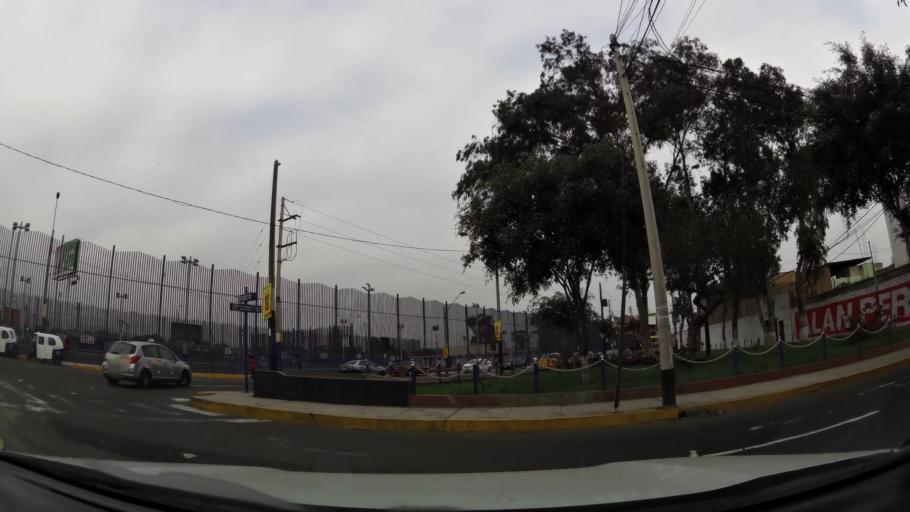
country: PE
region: Lima
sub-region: Lima
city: Surco
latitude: -12.1685
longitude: -77.0195
